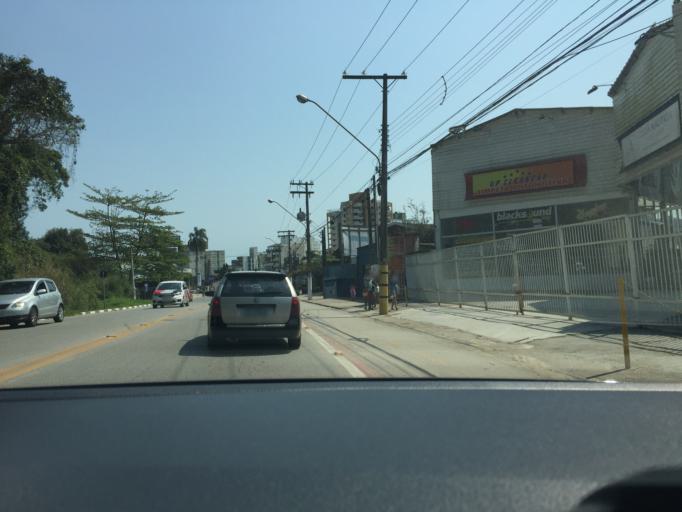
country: BR
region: Sao Paulo
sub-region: Guaruja
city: Guaruja
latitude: -23.9841
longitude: -46.1999
